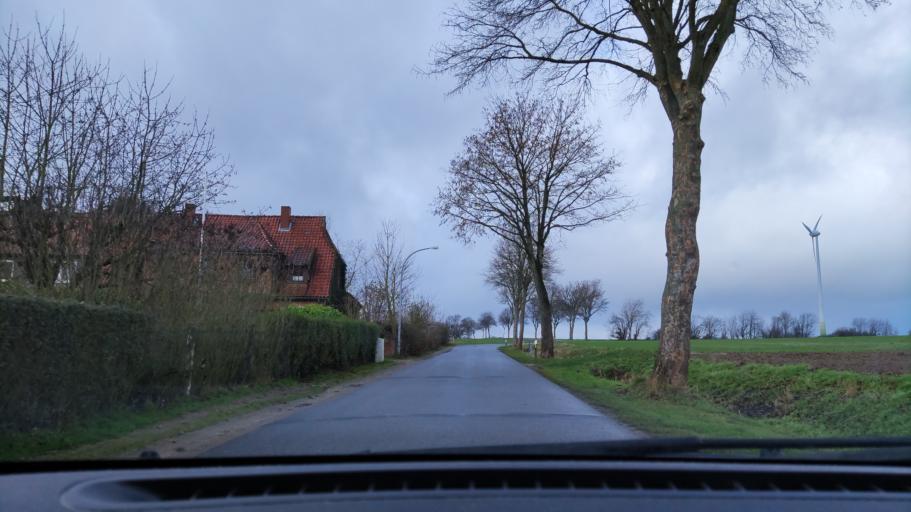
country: DE
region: Lower Saxony
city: Natendorf
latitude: 53.0830
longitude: 10.4591
